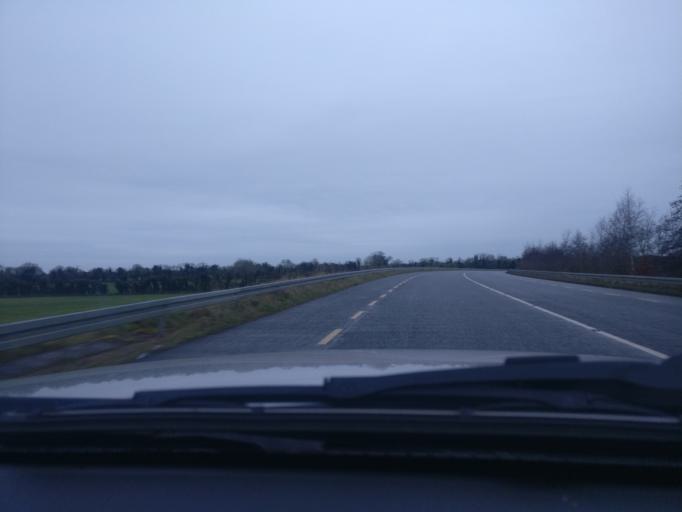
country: IE
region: Leinster
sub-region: An Mhi
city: Dunshaughlin
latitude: 53.5033
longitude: -6.5730
